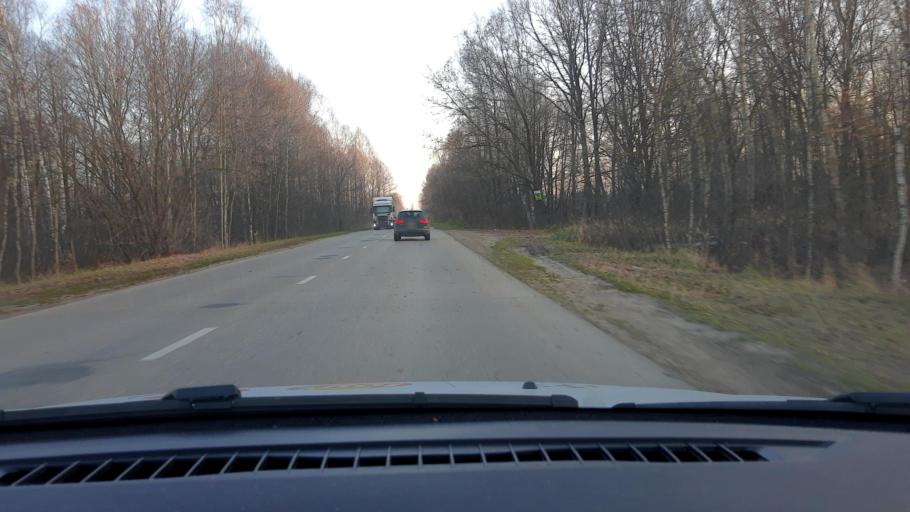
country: RU
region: Nizjnij Novgorod
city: Volodarsk
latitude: 56.2480
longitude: 43.1769
